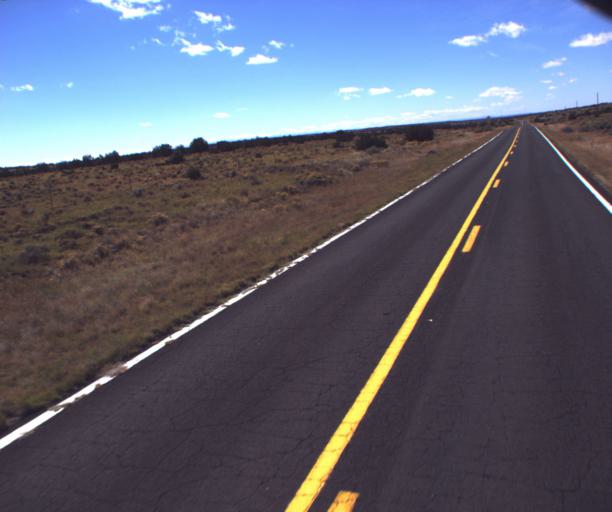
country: US
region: Arizona
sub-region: Apache County
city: Houck
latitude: 34.9545
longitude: -109.1625
